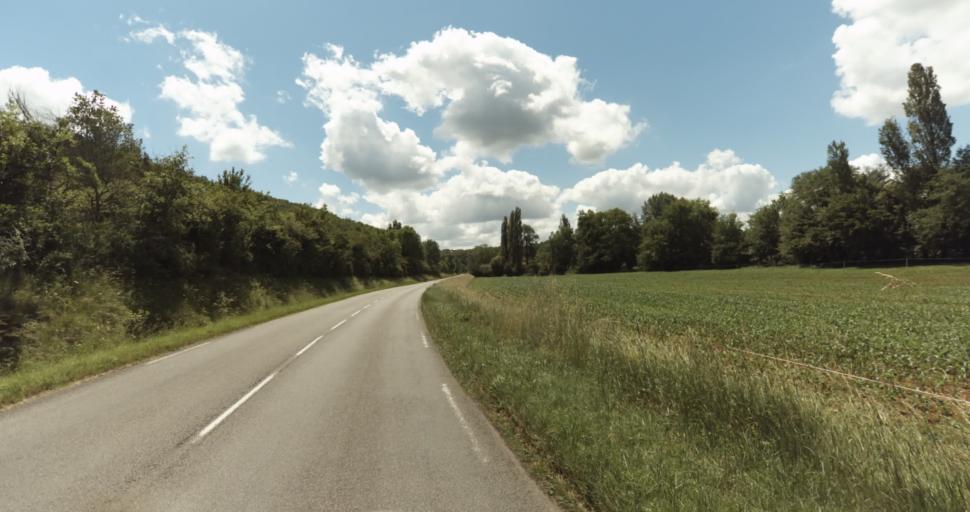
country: FR
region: Aquitaine
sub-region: Departement de la Dordogne
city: Beaumont-du-Perigord
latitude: 44.7917
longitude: 0.7580
